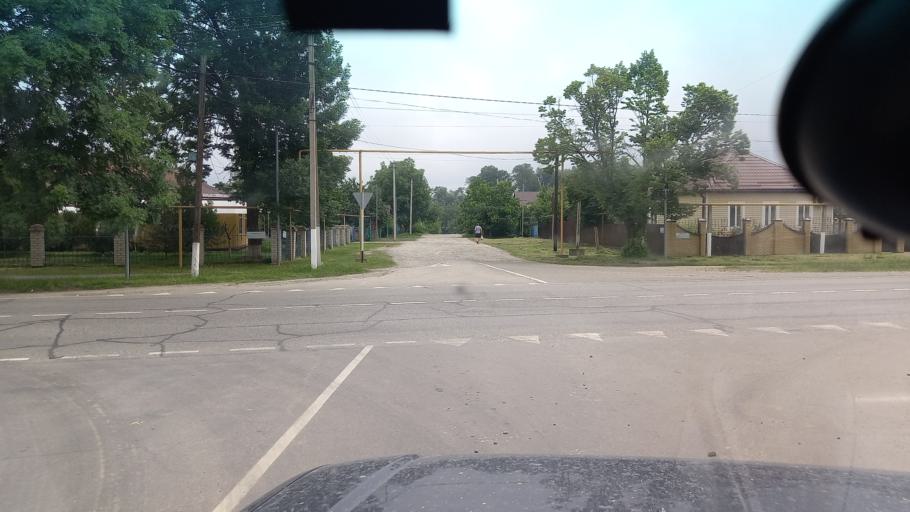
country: RU
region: Krasnodarskiy
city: Mostovskoy
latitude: 44.4162
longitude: 40.7992
